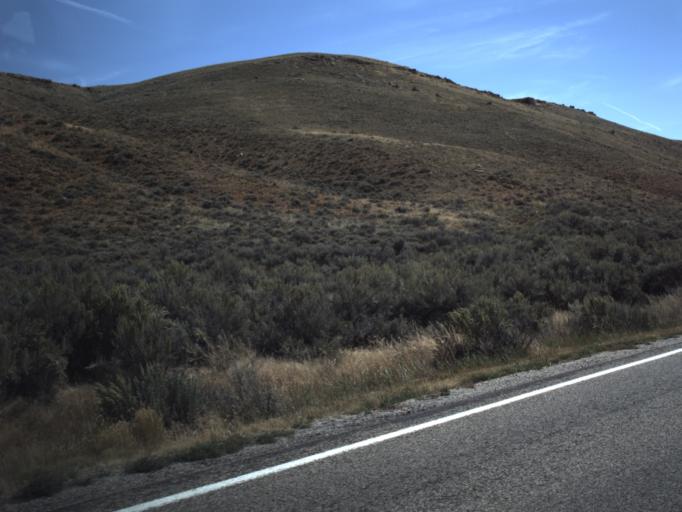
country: US
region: Utah
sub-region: Rich County
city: Randolph
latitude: 41.7745
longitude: -111.1783
